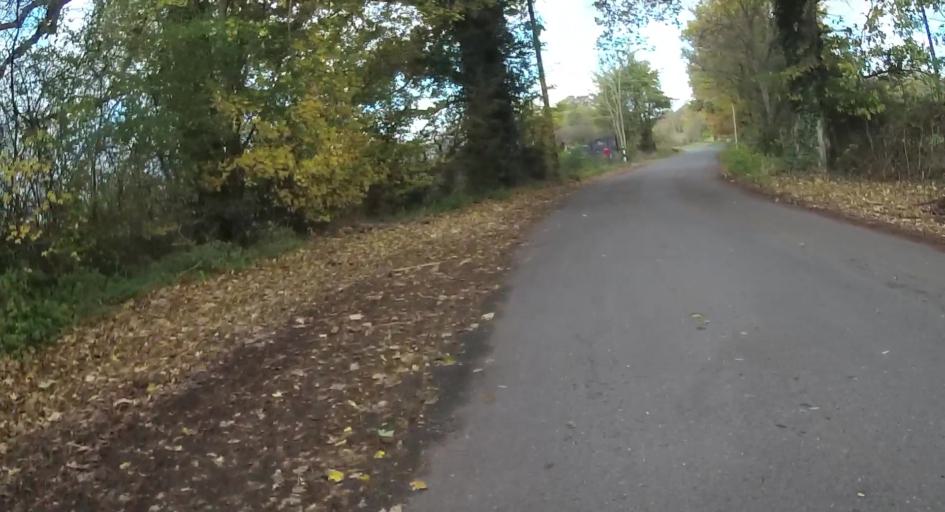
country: GB
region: England
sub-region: Hampshire
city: Basingstoke
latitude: 51.3198
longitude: -1.0719
